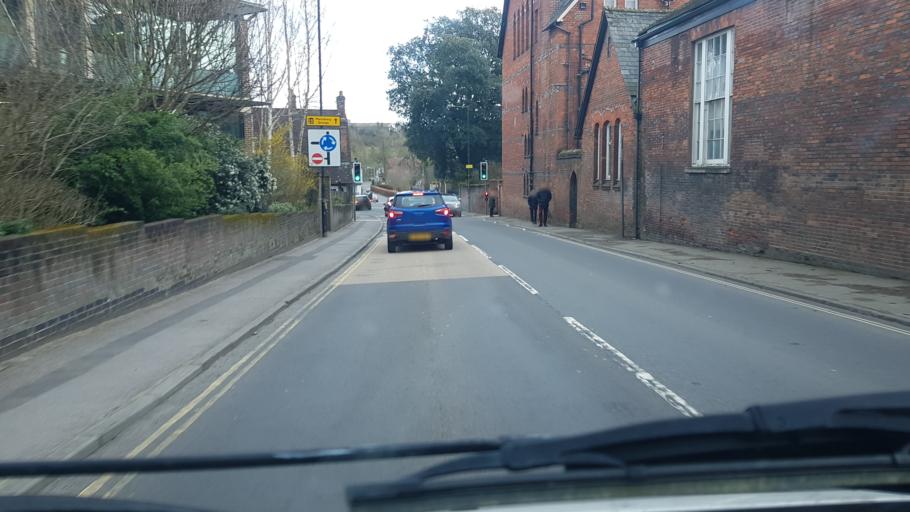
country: GB
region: England
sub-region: Wiltshire
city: Marlborough
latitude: 51.4179
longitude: -1.7355
